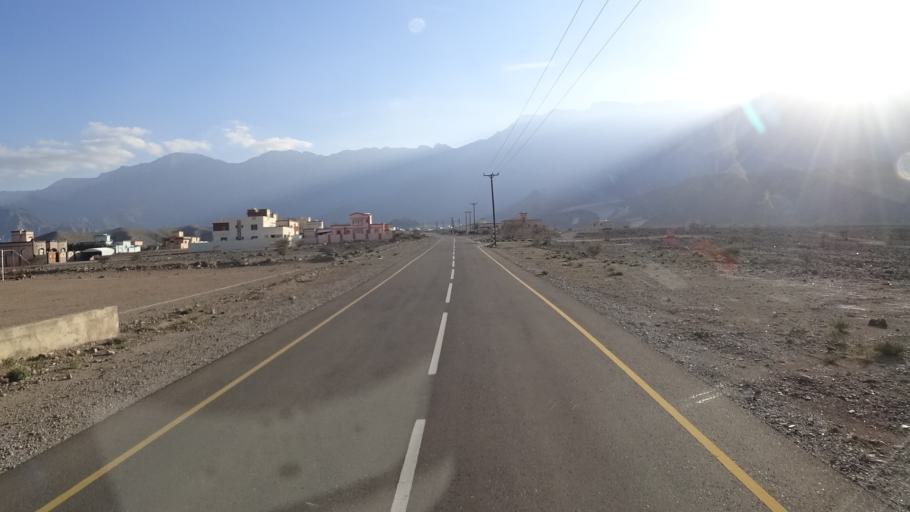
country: OM
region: Al Batinah
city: Rustaq
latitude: 23.2778
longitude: 57.3272
